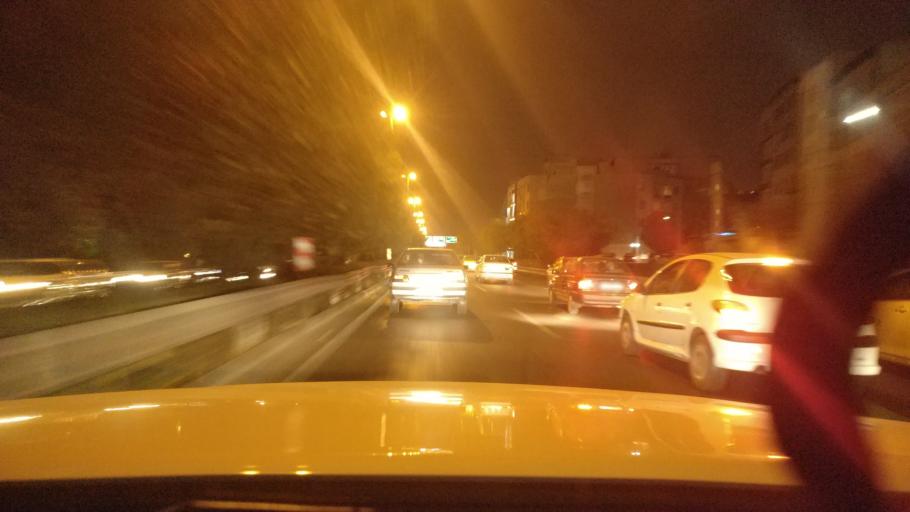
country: IR
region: Tehran
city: Tehran
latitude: 35.7387
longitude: 51.3264
